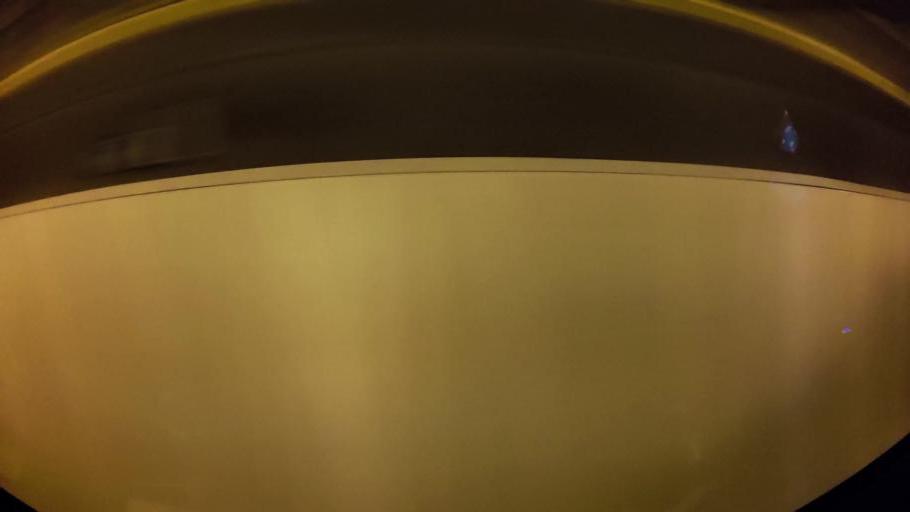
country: CL
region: Santiago Metropolitan
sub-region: Provincia de Santiago
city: Santiago
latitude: -33.4026
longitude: -70.6151
